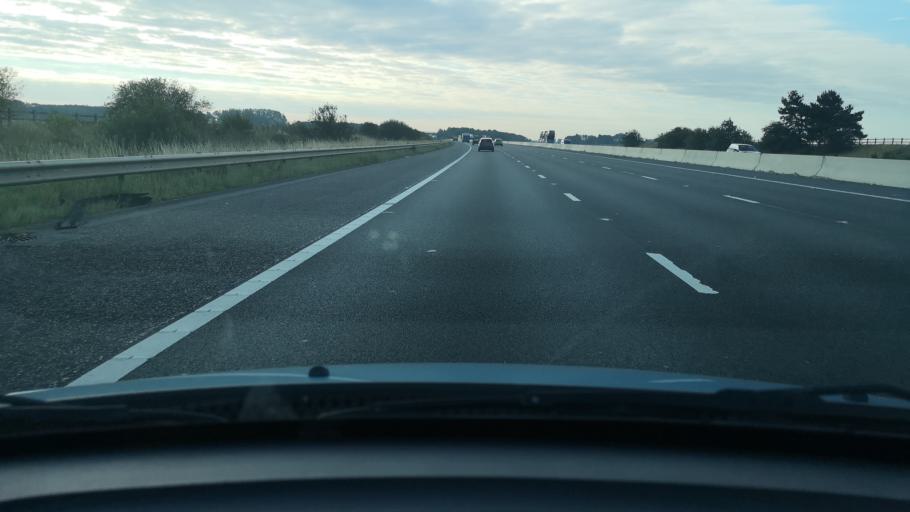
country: GB
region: England
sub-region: Doncaster
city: Hatfield
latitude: 53.5851
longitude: -0.9548
